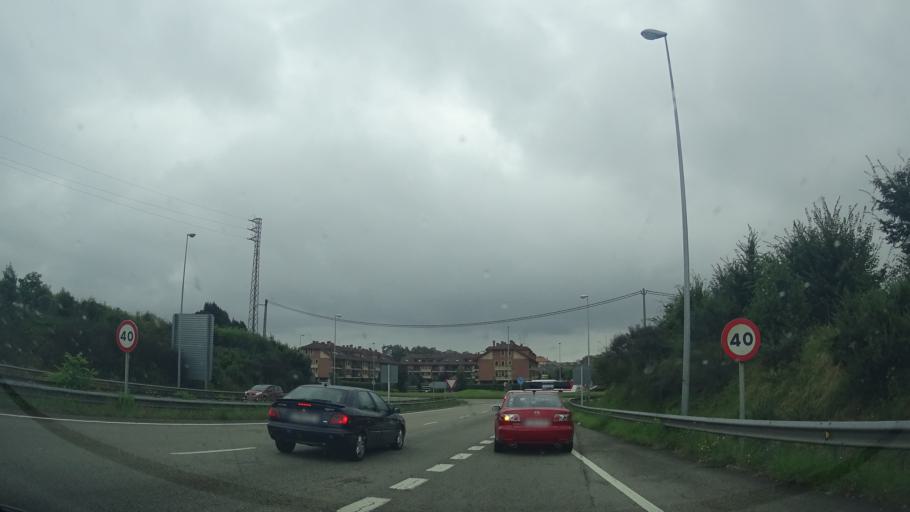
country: ES
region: Asturias
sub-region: Province of Asturias
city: Gijon
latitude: 43.5241
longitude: -5.6389
